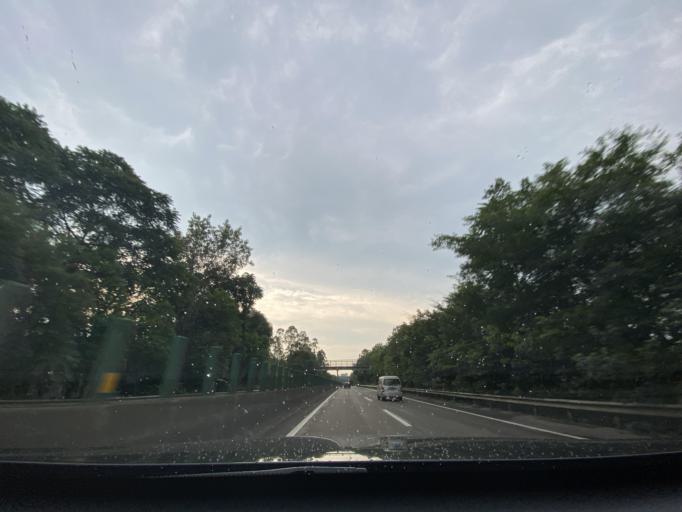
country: CN
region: Sichuan
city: Chonglong
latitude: 29.7780
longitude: 104.7407
